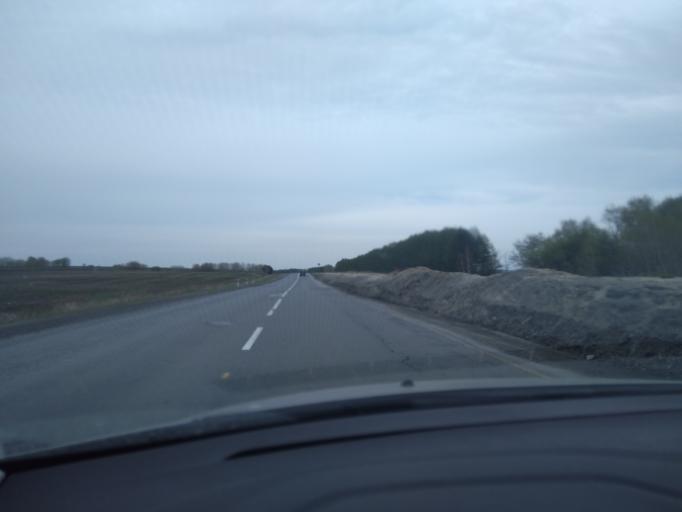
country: RU
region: Sverdlovsk
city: Kamyshlov
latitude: 56.8489
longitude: 62.8479
